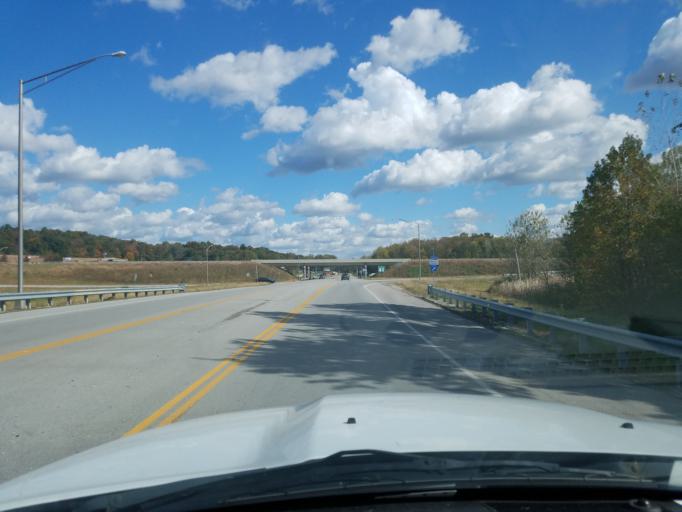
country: US
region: Kentucky
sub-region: Butler County
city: Morgantown
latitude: 37.2018
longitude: -86.7031
